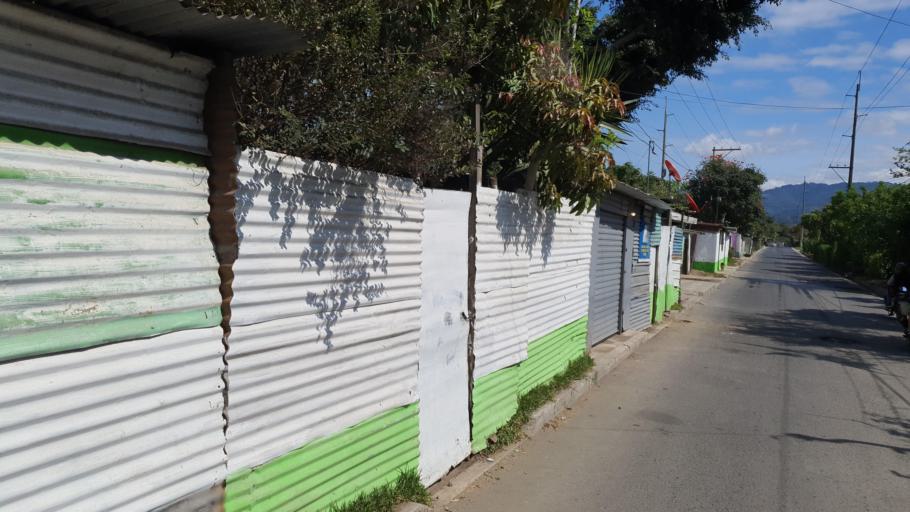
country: GT
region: Guatemala
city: Villa Canales
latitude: 14.4599
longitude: -90.5559
